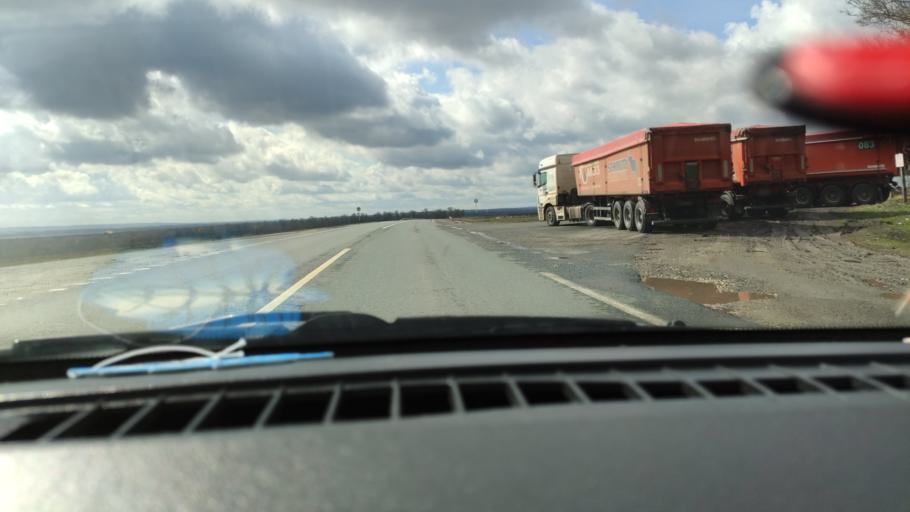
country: RU
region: Samara
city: Yelkhovka
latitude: 53.8626
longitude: 50.2568
